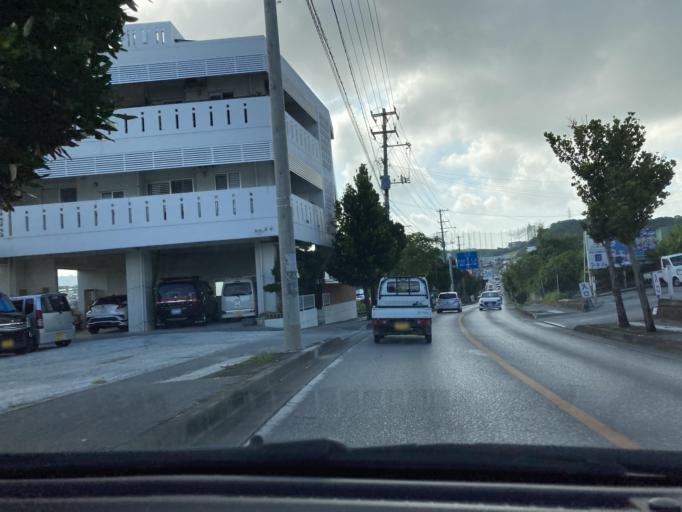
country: JP
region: Okinawa
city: Tomigusuku
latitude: 26.1715
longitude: 127.7369
